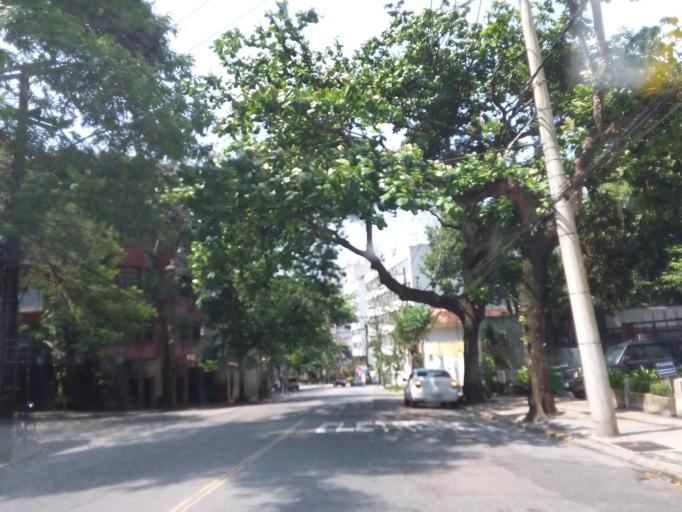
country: BR
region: Rio de Janeiro
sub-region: Rio De Janeiro
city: Rio de Janeiro
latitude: -22.9814
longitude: -43.2363
